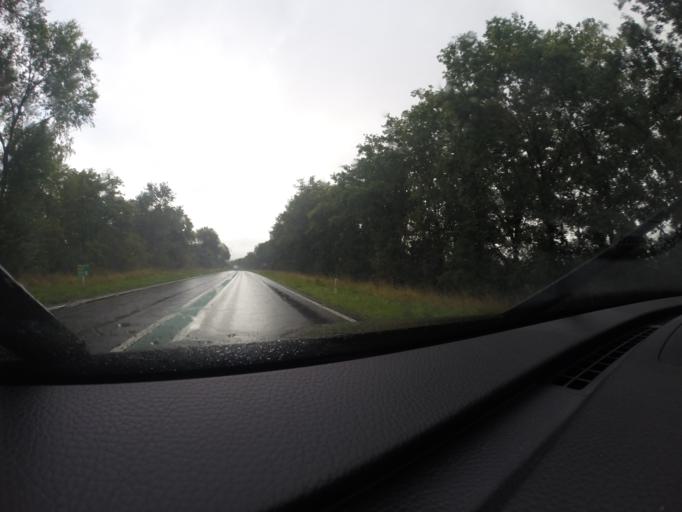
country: NL
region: Gelderland
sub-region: Gemeente Lochem
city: Laren
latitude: 52.2213
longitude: 6.3924
